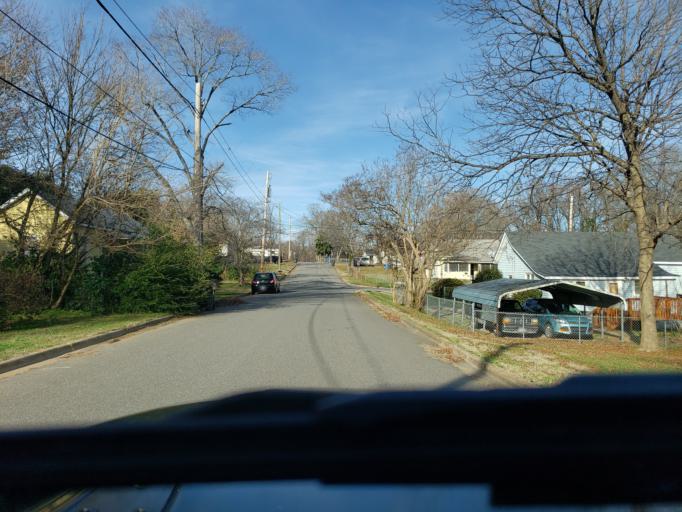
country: US
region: North Carolina
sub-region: Cleveland County
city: Kings Mountain
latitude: 35.2462
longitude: -81.3346
